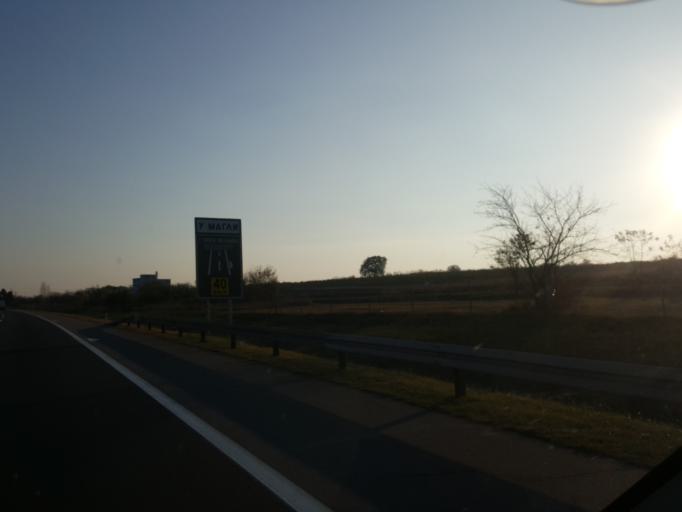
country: RS
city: Lugavcina
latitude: 44.5698
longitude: 20.9803
